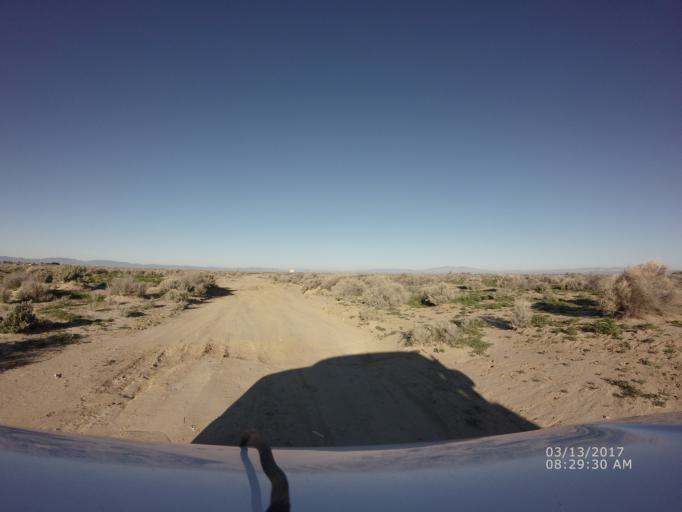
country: US
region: California
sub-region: Los Angeles County
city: Lake Los Angeles
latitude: 34.7343
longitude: -117.9424
